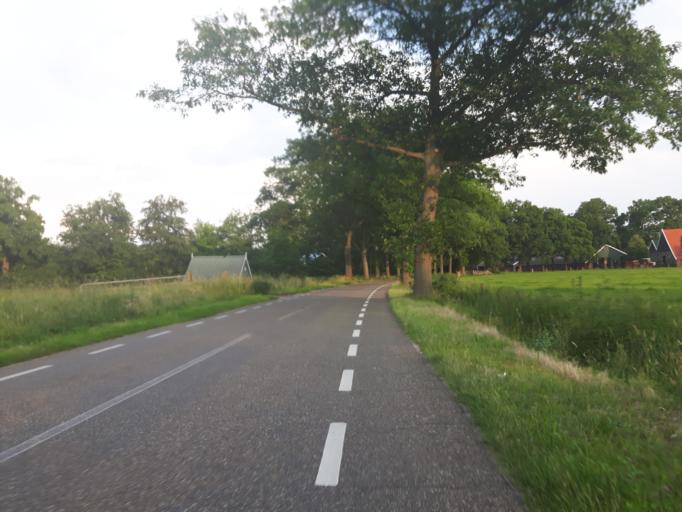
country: NL
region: Overijssel
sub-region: Gemeente Hengelo
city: Hengelo
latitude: 52.2366
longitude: 6.8261
